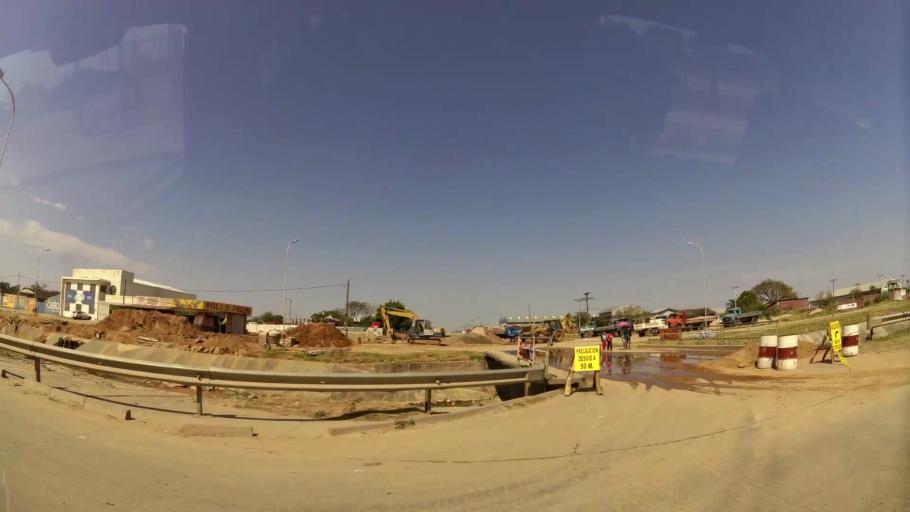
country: BO
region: Santa Cruz
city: Santa Cruz de la Sierra
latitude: -17.7373
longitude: -63.1422
